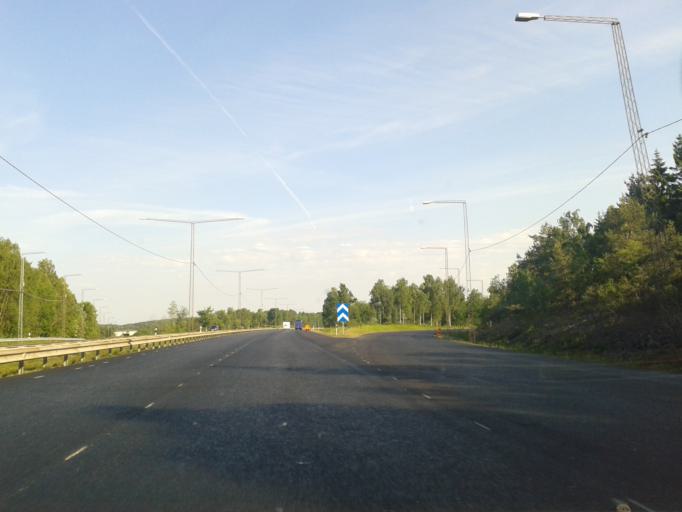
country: SE
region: Vaestra Goetaland
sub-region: Kungalvs Kommun
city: Kode
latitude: 57.9423
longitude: 11.8601
